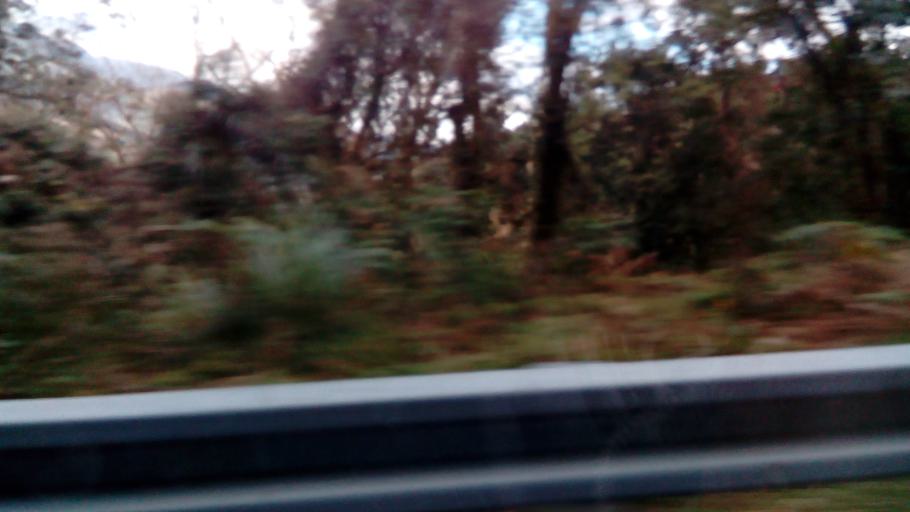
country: TW
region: Taiwan
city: Daxi
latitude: 24.4050
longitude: 121.3641
